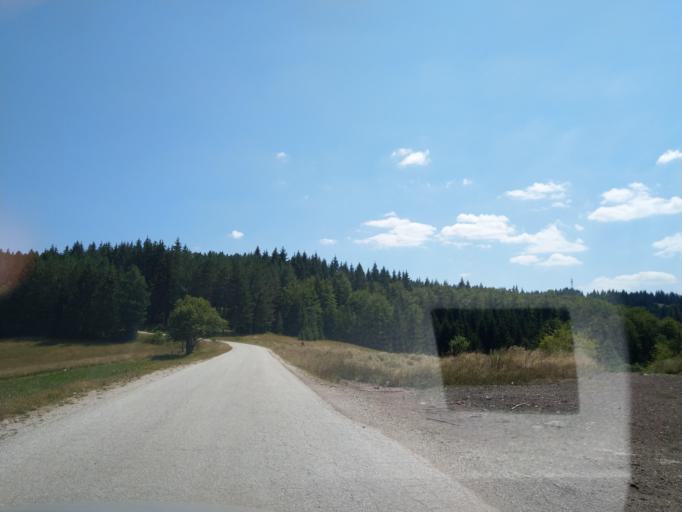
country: RS
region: Central Serbia
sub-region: Zlatiborski Okrug
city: Nova Varos
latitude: 43.4693
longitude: 19.9671
